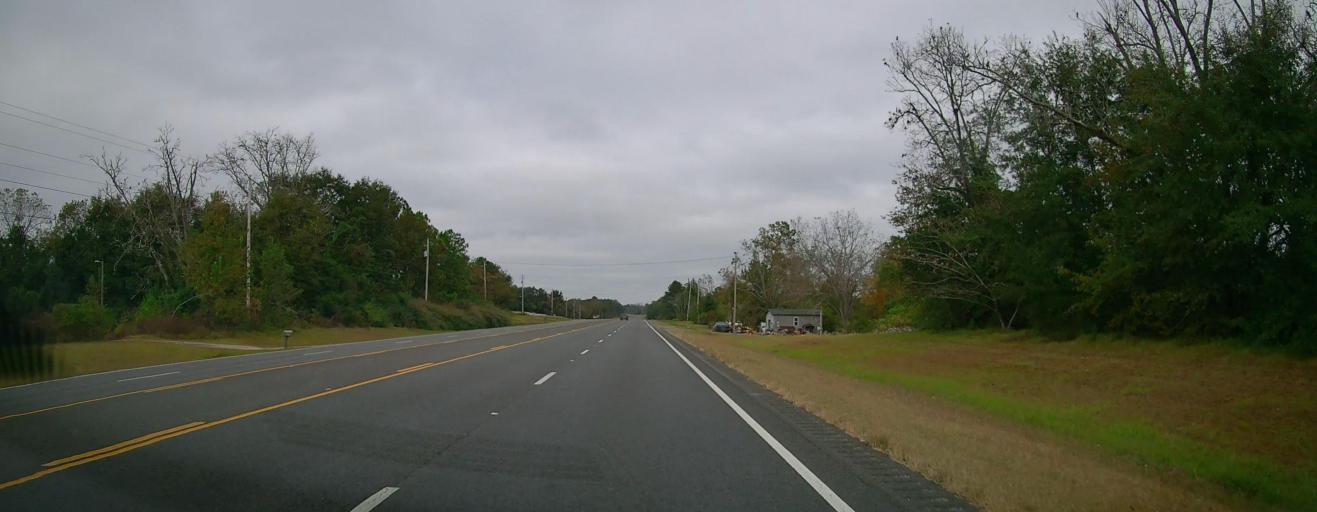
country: US
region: Georgia
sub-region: Thomas County
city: Thomasville
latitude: 30.9280
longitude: -83.9125
